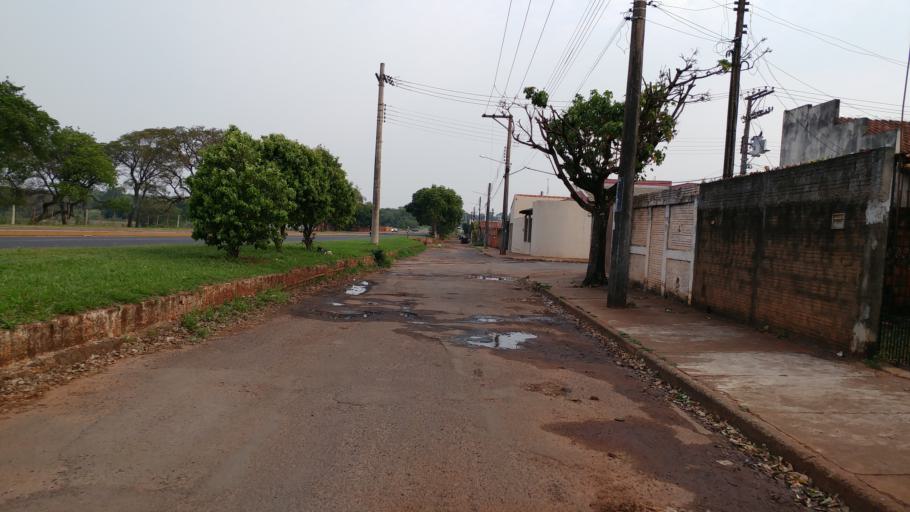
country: BR
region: Sao Paulo
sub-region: Paraguacu Paulista
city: Paraguacu Paulista
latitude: -22.4389
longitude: -50.5813
